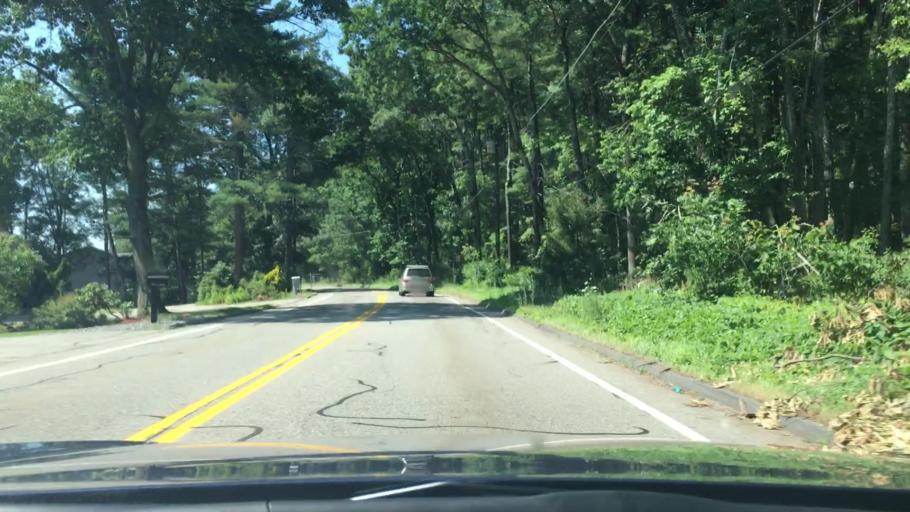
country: US
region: Massachusetts
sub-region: Middlesex County
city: Billerica
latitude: 42.5699
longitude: -71.2965
